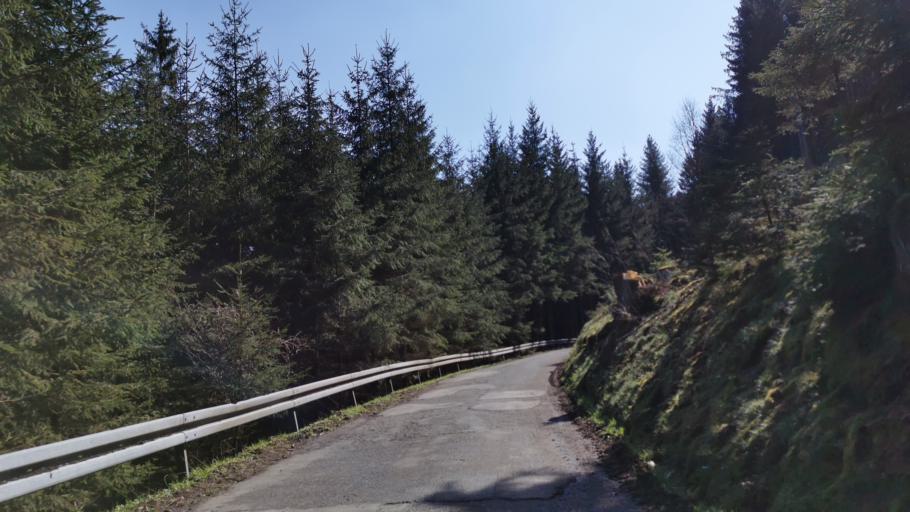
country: DE
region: Thuringia
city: Probstzella
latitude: 50.5138
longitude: 11.4104
